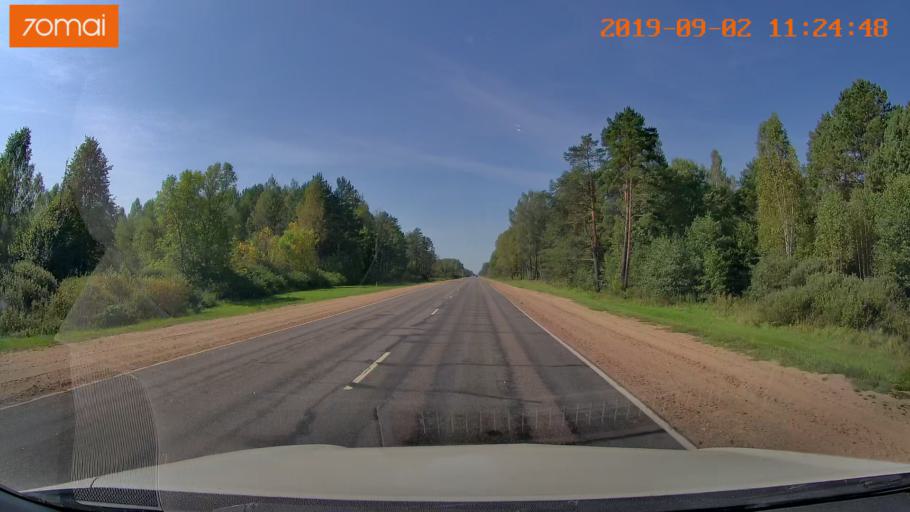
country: RU
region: Smolensk
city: Roslavl'
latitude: 54.0072
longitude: 32.9674
